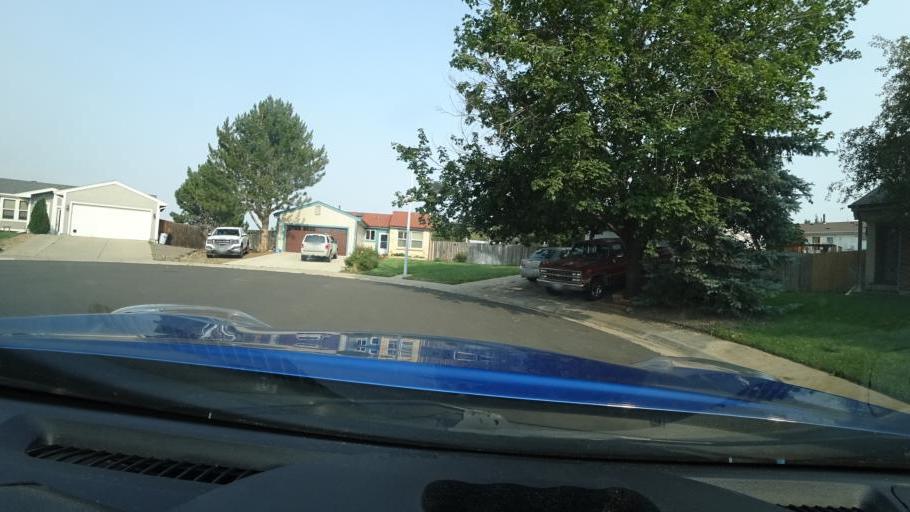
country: US
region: Colorado
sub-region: Adams County
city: Aurora
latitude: 39.6669
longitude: -104.7800
